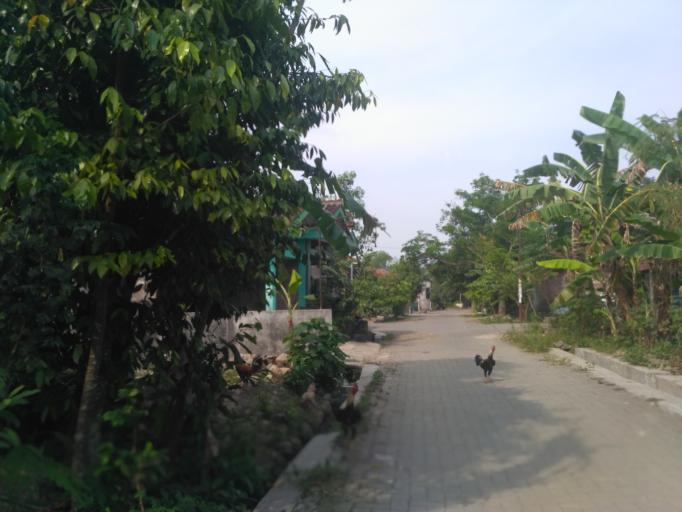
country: ID
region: Central Java
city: Mranggen
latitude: -7.0193
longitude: 110.4833
